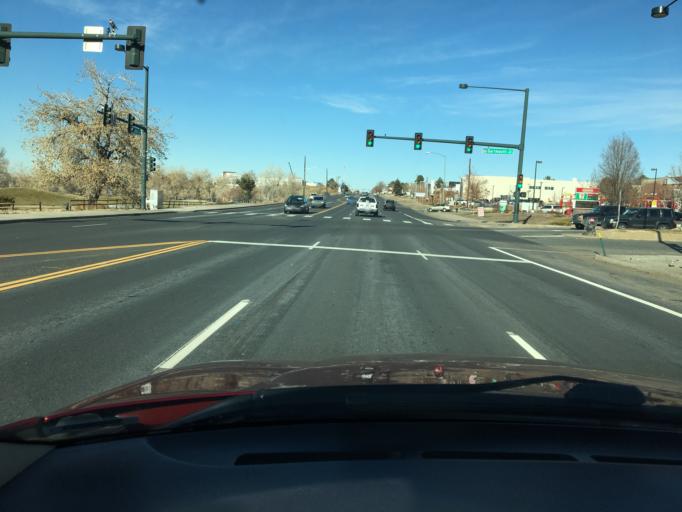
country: US
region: Colorado
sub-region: Adams County
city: Aurora
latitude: 39.6600
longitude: -104.8663
